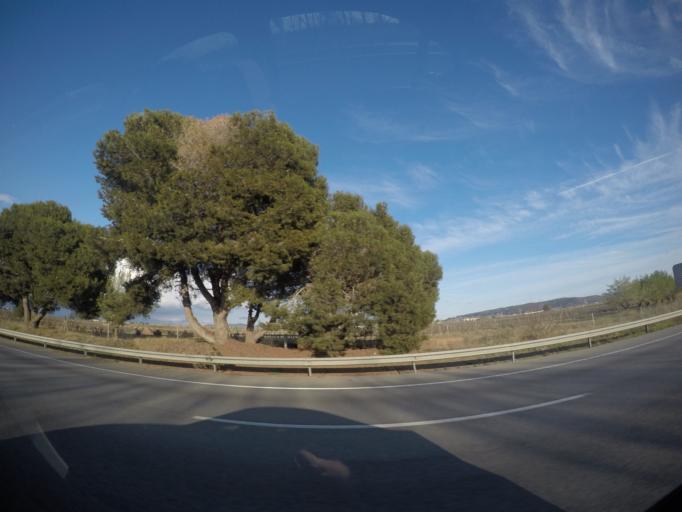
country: ES
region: Catalonia
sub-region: Provincia de Barcelona
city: La Granada
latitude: 41.3603
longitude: 1.7256
